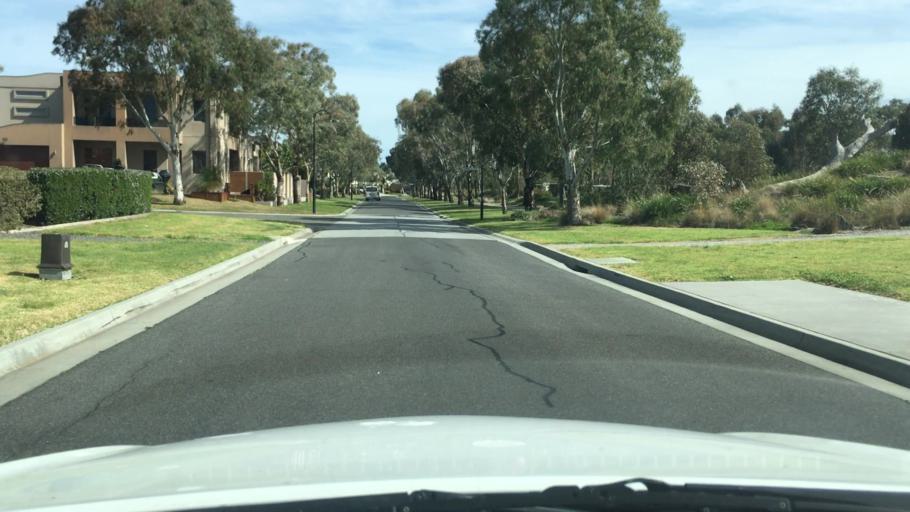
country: AU
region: Victoria
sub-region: Kingston
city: Waterways
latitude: -38.0132
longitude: 145.1373
